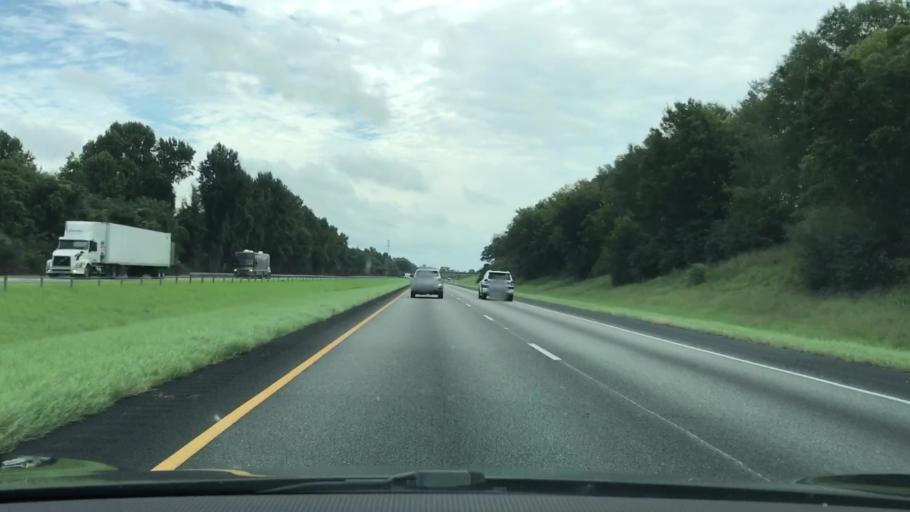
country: US
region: Alabama
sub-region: Elmore County
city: Tallassee
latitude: 32.4134
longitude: -85.9488
